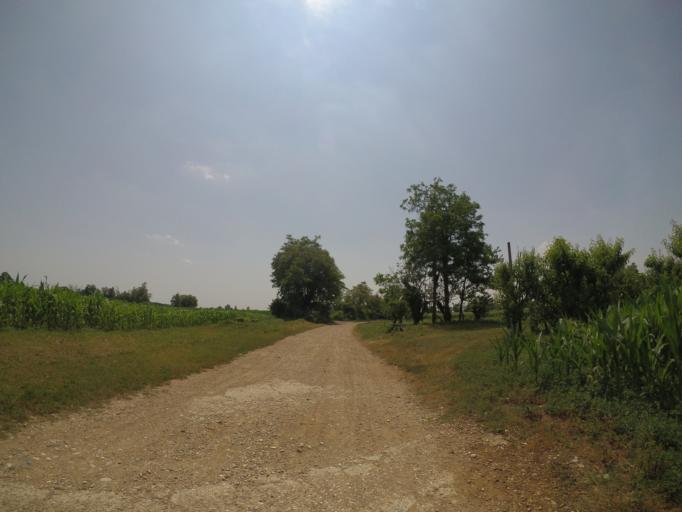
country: IT
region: Friuli Venezia Giulia
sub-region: Provincia di Udine
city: Bertiolo
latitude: 45.9645
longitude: 13.0675
